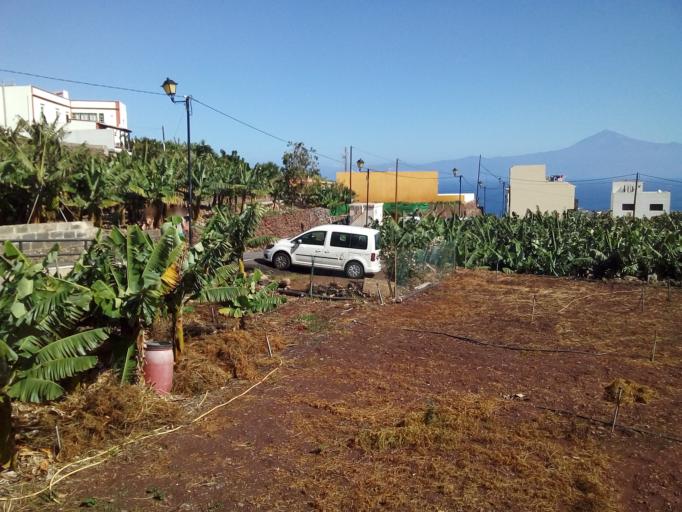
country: ES
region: Canary Islands
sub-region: Provincia de Santa Cruz de Tenerife
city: Agulo
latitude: 28.1880
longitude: -17.1938
